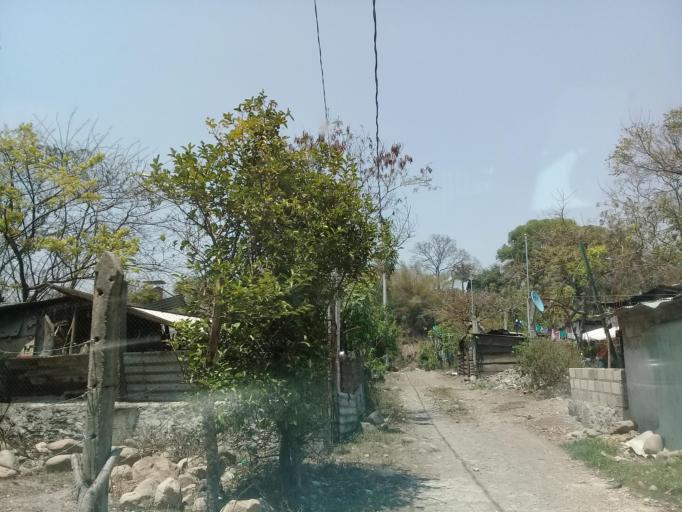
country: MX
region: Veracruz
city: Paraje Nuevo
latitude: 18.8712
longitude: -96.8676
